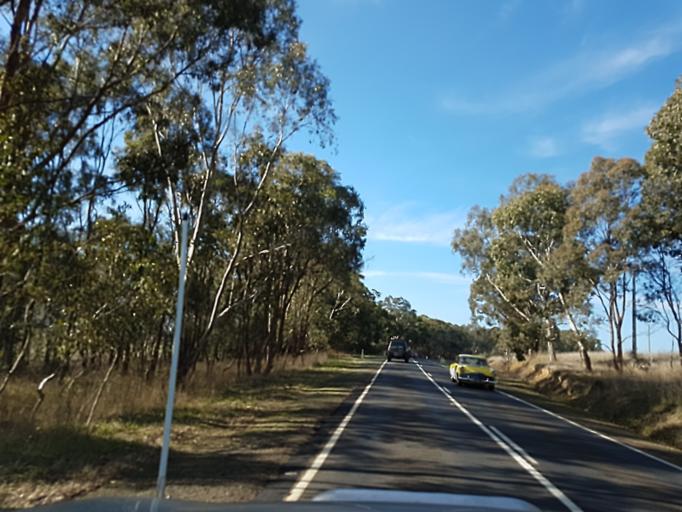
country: AU
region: Victoria
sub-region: Murrindindi
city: Alexandra
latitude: -37.1439
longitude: 145.6215
